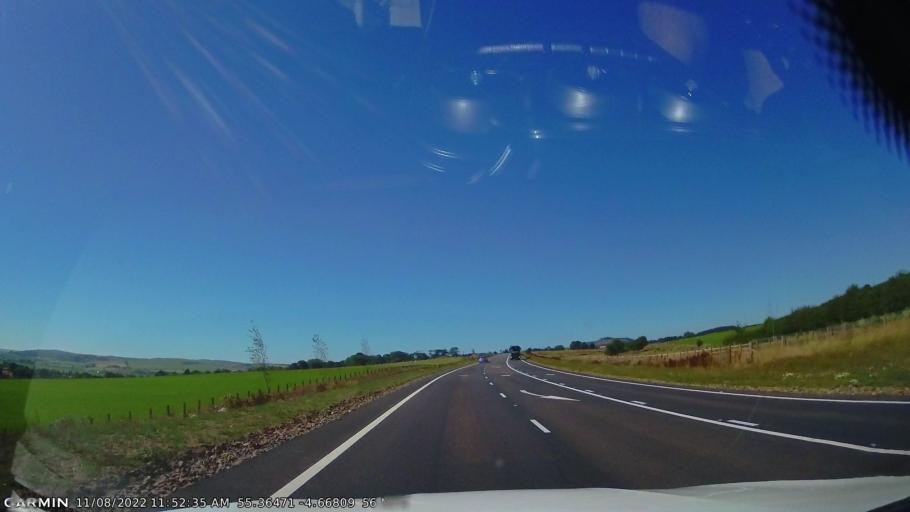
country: GB
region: Scotland
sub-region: South Ayrshire
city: Maybole
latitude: 55.3649
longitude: -4.6678
